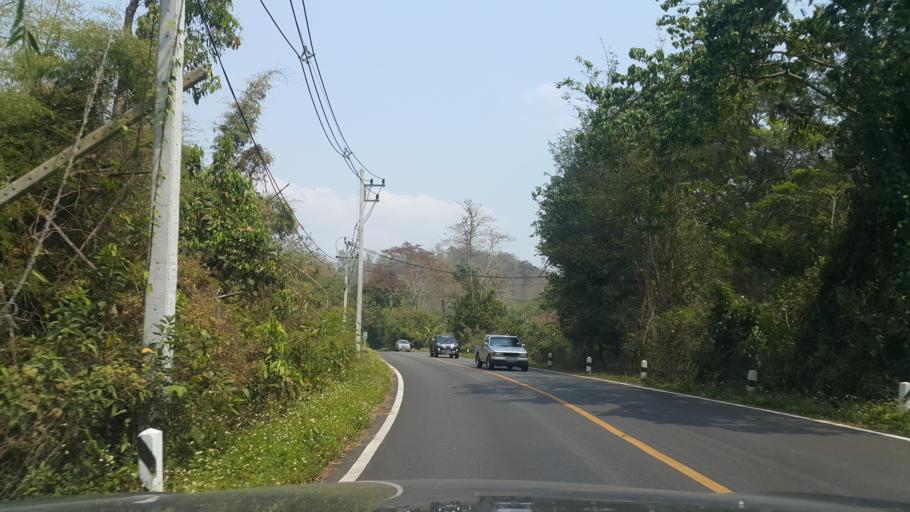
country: TH
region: Lamphun
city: Thung Hua Chang
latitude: 17.9012
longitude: 99.1323
